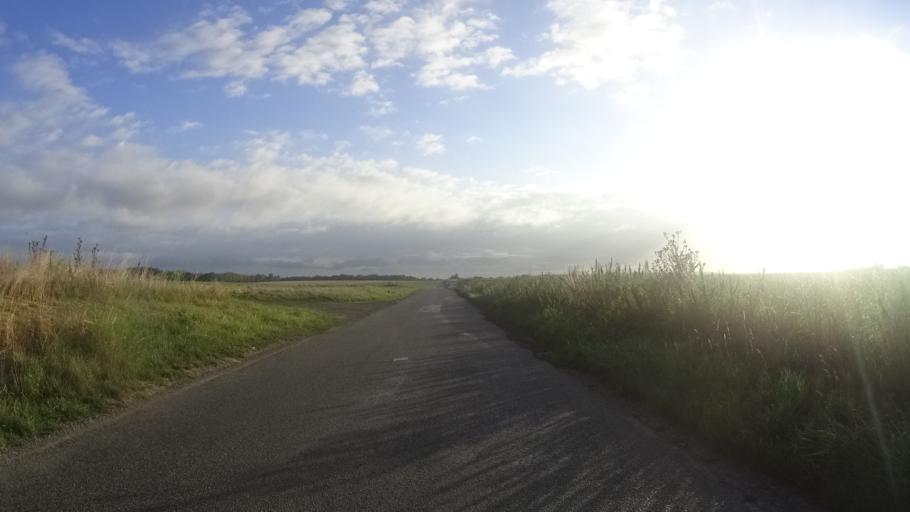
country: FR
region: Picardie
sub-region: Departement de l'Oise
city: Chamant
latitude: 49.2261
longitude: 2.6734
